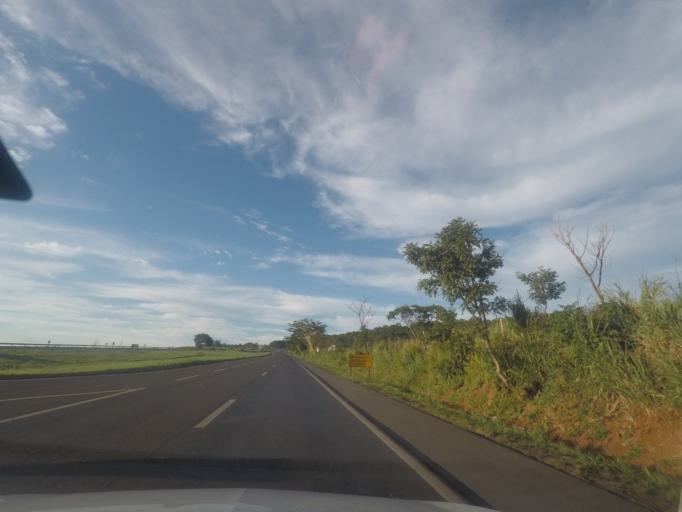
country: BR
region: Goias
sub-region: Goiatuba
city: Goiatuba
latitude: -18.0824
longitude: -49.2705
